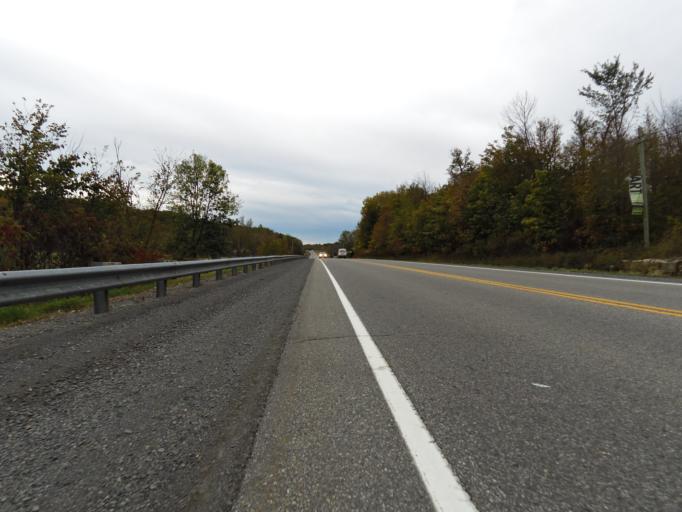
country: CA
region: Ontario
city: Gananoque
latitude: 44.3893
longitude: -76.3224
